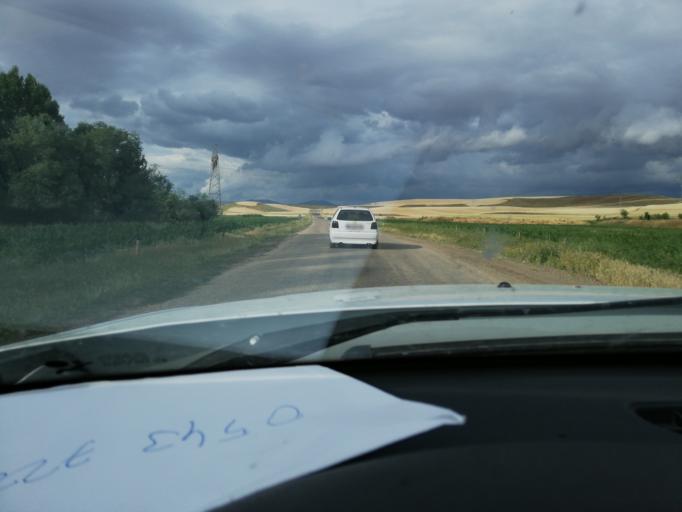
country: TR
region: Kirsehir
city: Kirsehir
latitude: 39.0281
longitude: 34.1316
